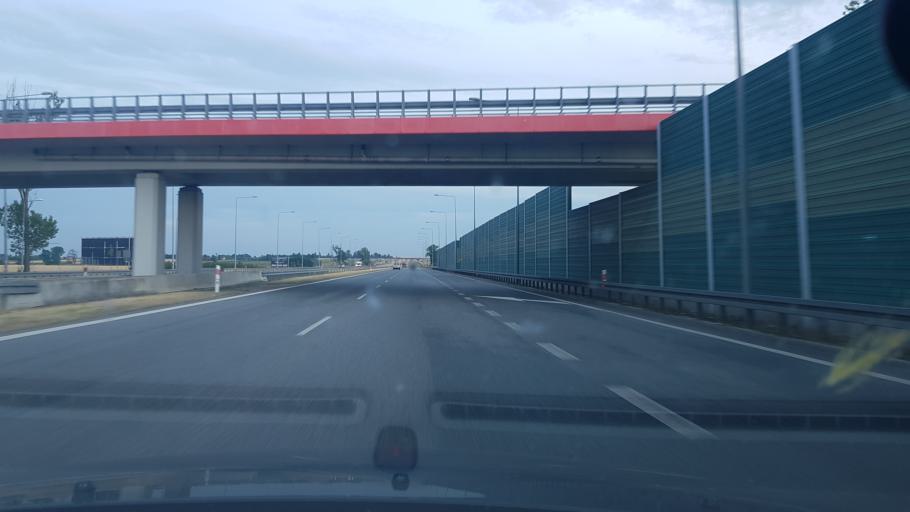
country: PL
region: Lodz Voivodeship
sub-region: Powiat kutnowski
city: Krzyzanow
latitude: 52.1827
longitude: 19.4870
